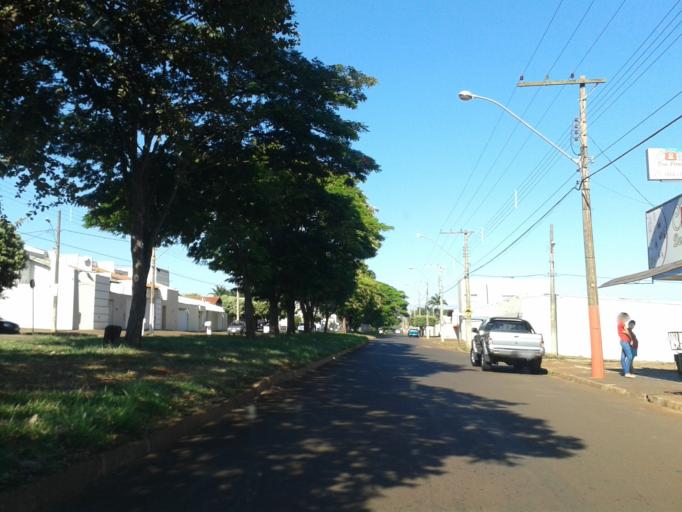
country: BR
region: Minas Gerais
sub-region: Ituiutaba
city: Ituiutaba
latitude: -18.9787
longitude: -49.4868
